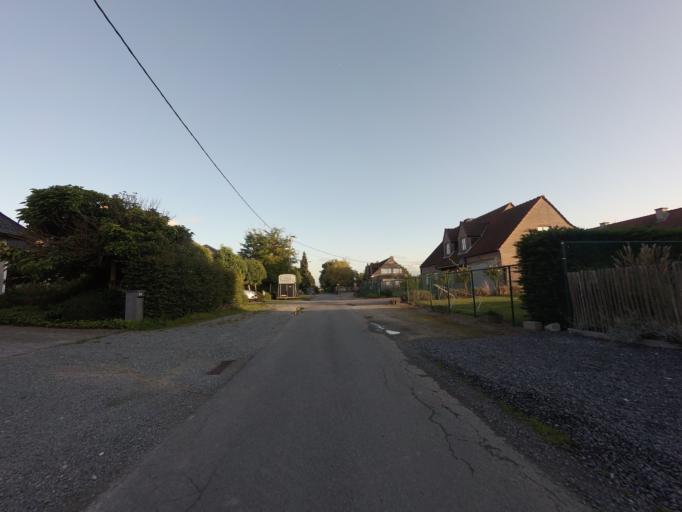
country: BE
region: Flanders
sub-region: Provincie Vlaams-Brabant
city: Londerzeel
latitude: 50.9930
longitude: 4.3272
